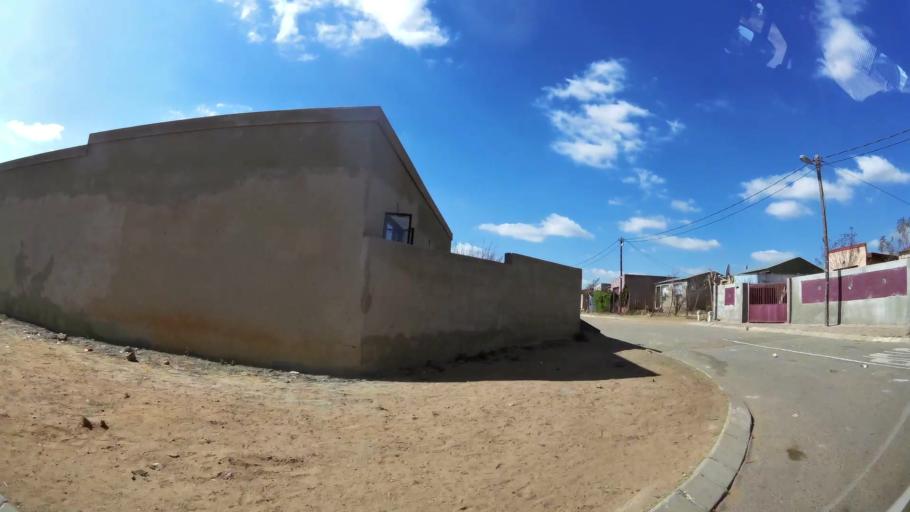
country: ZA
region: Gauteng
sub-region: West Rand District Municipality
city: Krugersdorp
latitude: -26.1438
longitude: 27.7871
